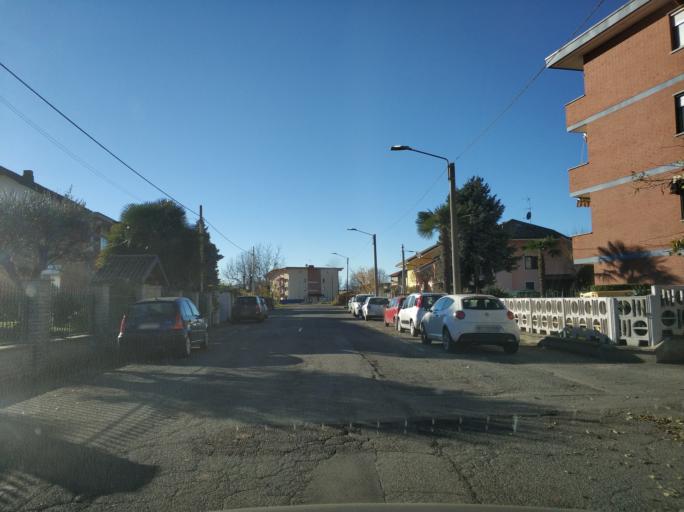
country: IT
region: Piedmont
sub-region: Provincia di Torino
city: Cirie
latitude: 45.2286
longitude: 7.6133
